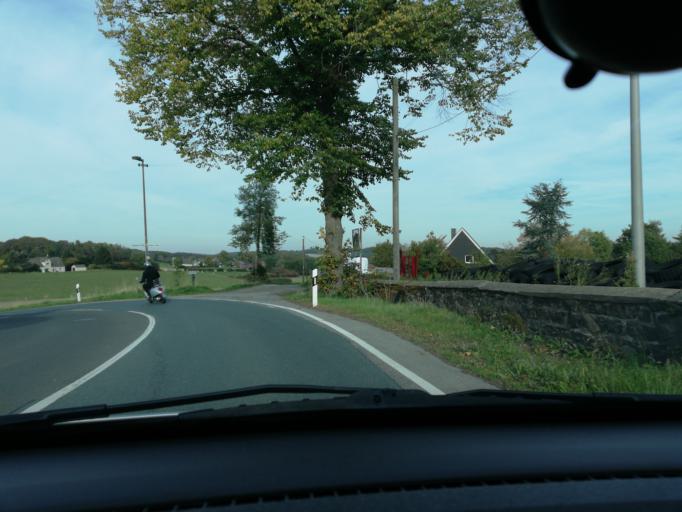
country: DE
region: North Rhine-Westphalia
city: Sprockhovel
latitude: 51.3401
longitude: 7.2593
